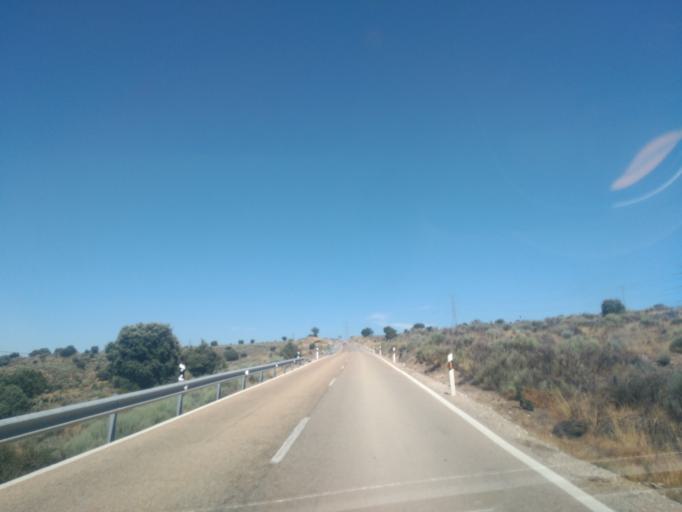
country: ES
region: Castille and Leon
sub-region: Provincia de Zamora
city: Villardeciervos
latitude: 41.9887
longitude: -6.2397
